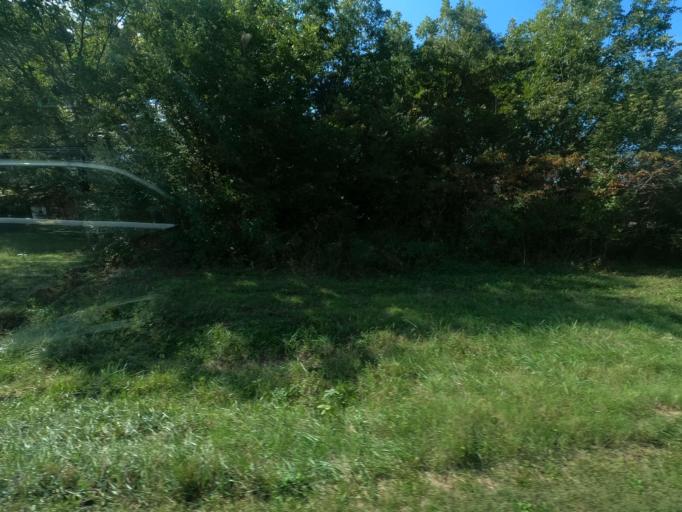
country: US
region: Illinois
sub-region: Massac County
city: Metropolis
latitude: 37.1951
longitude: -88.7292
